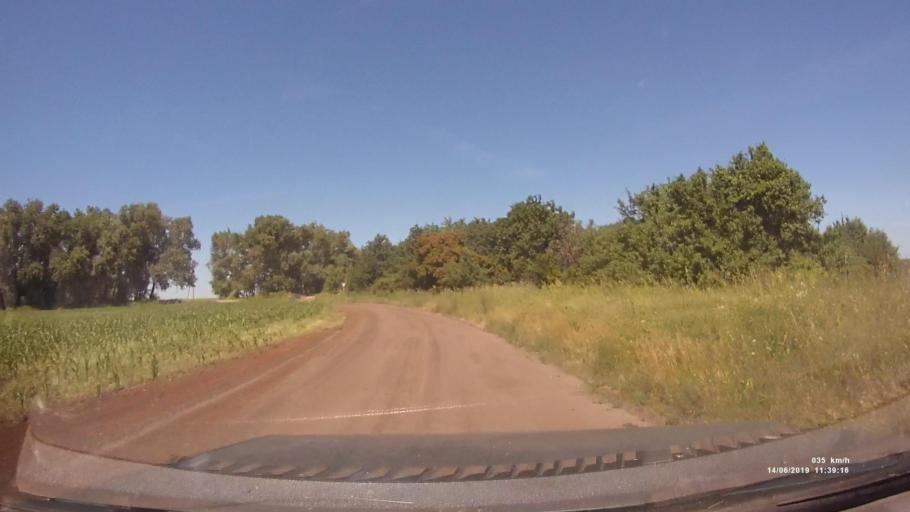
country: RU
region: Rostov
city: Kazanskaya
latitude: 49.8693
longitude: 41.3669
